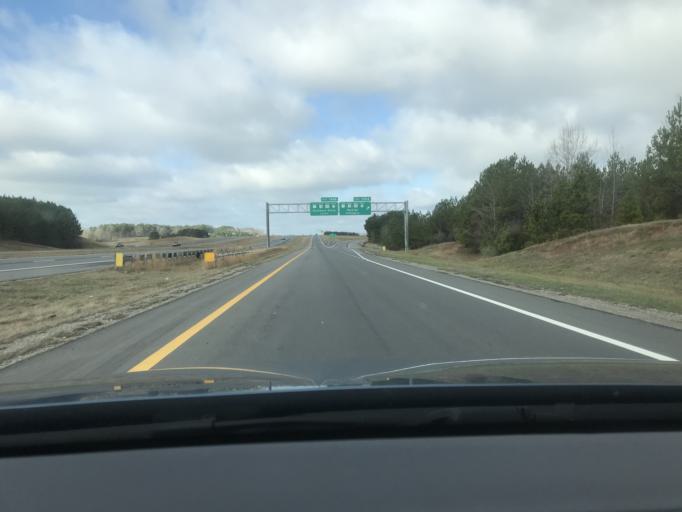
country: US
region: North Carolina
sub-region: Lee County
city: Sanford
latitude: 35.5095
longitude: -79.1808
